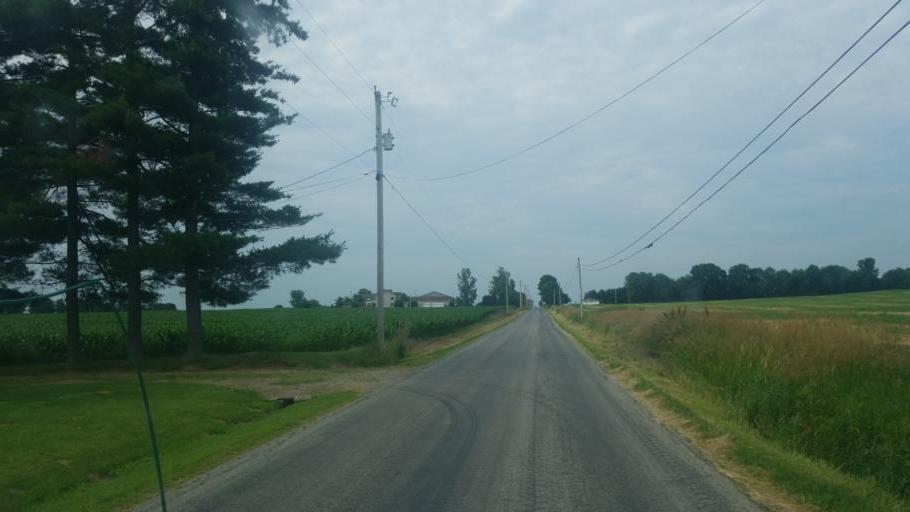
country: US
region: Ohio
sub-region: Wayne County
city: Wooster
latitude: 40.7965
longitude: -82.0229
